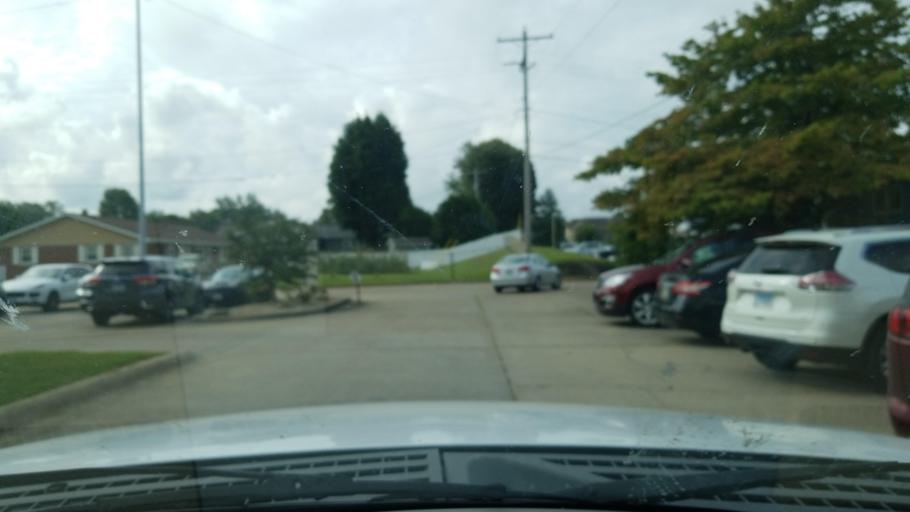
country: US
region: Illinois
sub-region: Saline County
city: Harrisburg
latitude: 37.7306
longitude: -88.5241
